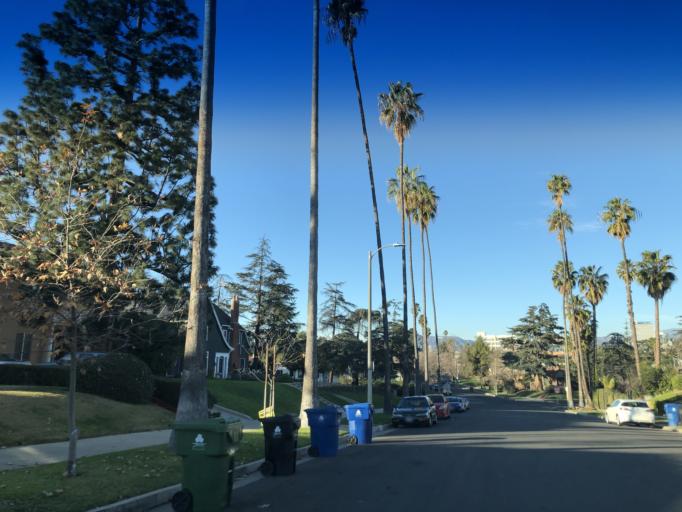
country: US
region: California
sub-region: Los Angeles County
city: Hollywood
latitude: 34.0486
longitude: -118.3131
